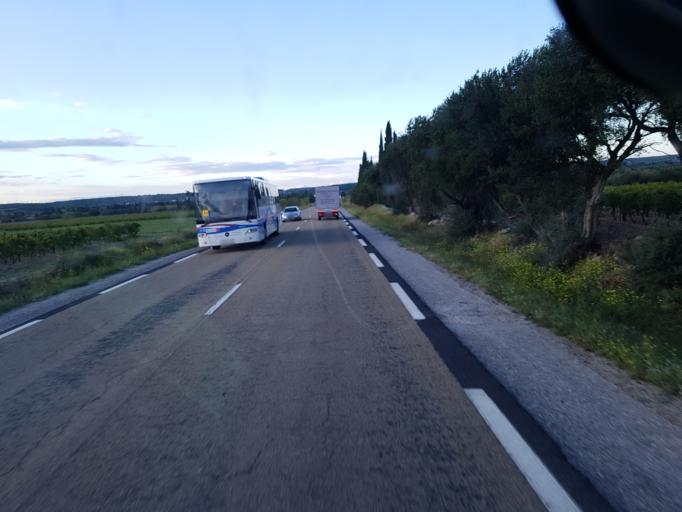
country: FR
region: Languedoc-Roussillon
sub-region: Departement de l'Aude
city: Leucate
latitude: 42.9520
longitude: 2.9866
